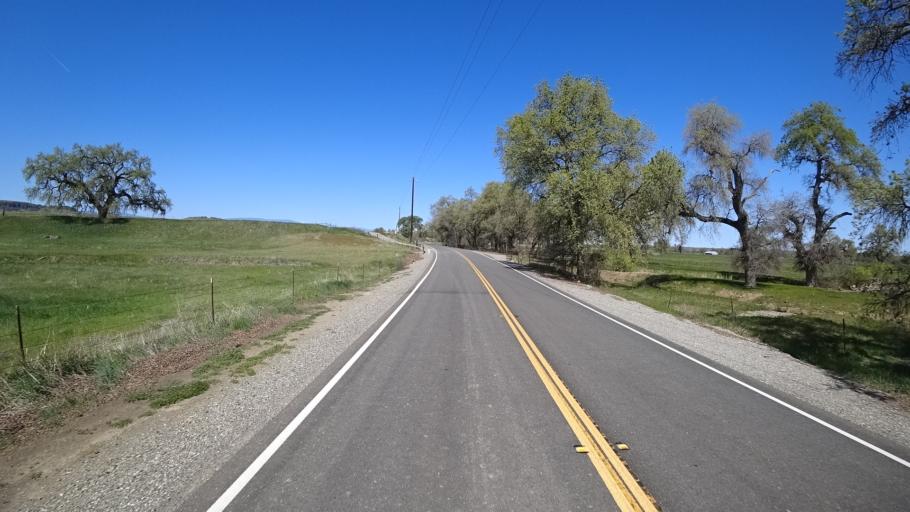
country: US
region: California
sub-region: Glenn County
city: Orland
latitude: 39.7931
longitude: -122.3125
